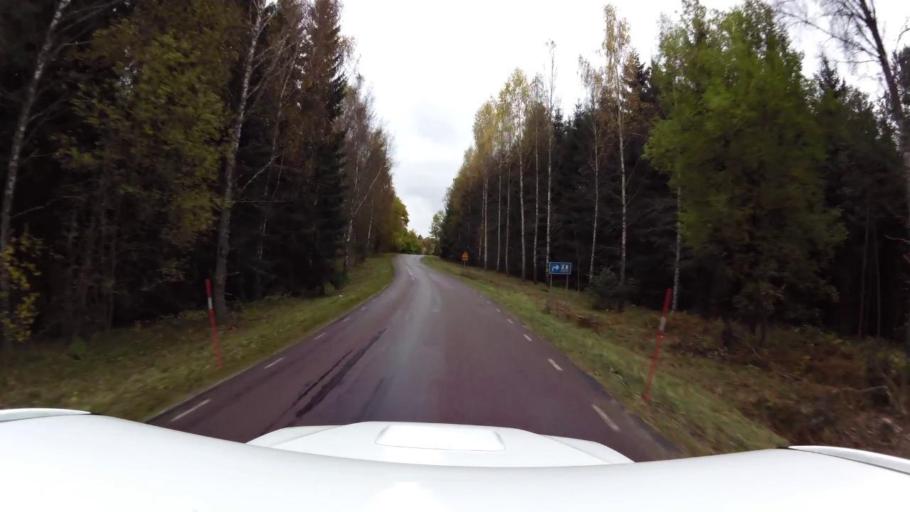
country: SE
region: OEstergoetland
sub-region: Linkopings Kommun
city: Ljungsbro
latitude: 58.5753
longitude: 15.5108
